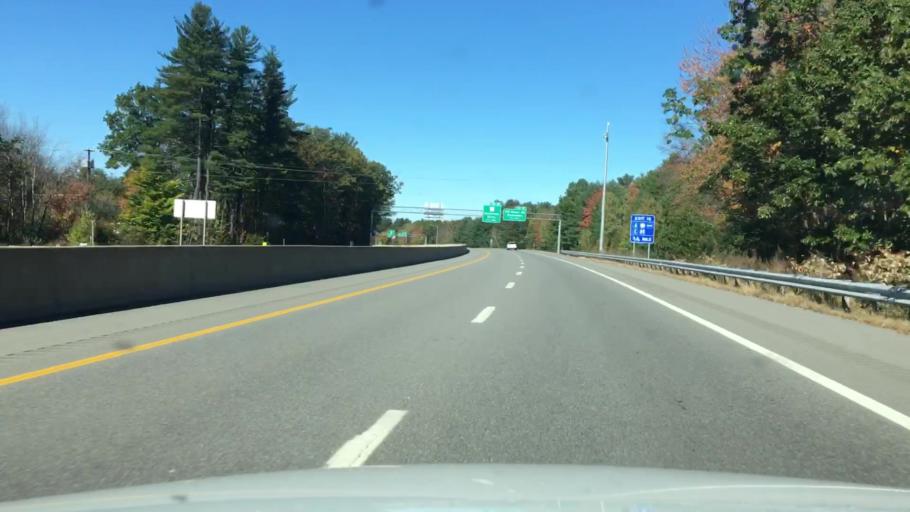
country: US
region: New Hampshire
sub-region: Strafford County
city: Rochester
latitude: 43.2772
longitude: -70.9674
